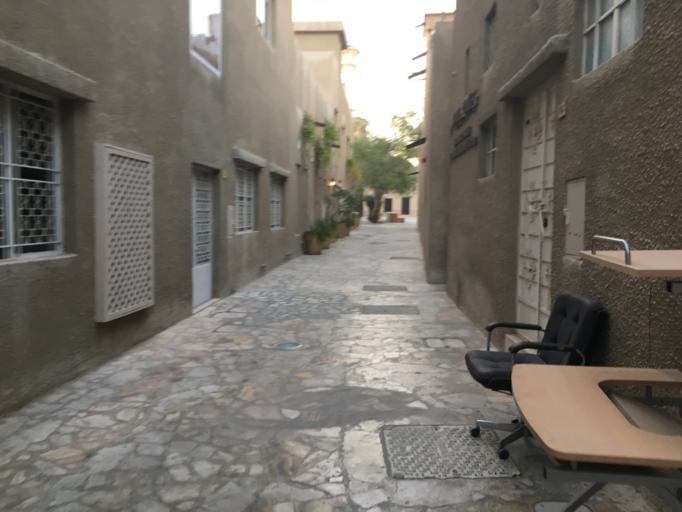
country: AE
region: Ash Shariqah
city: Sharjah
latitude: 25.2638
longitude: 55.3001
